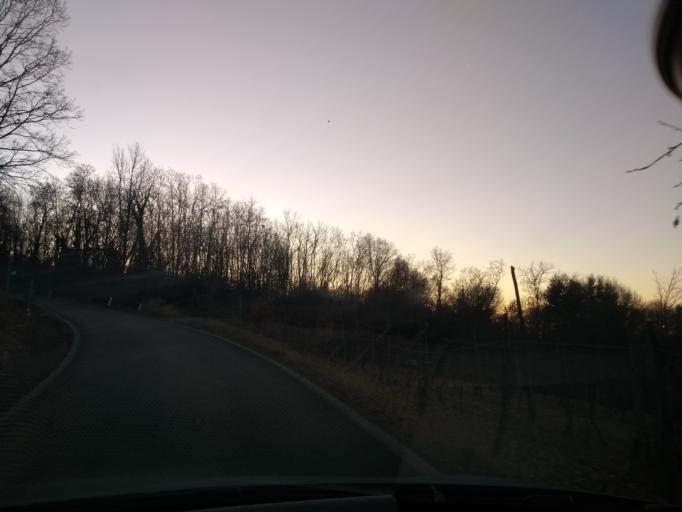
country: IT
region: Piedmont
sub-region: Provincia di Torino
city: Balangero
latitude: 45.2740
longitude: 7.5275
